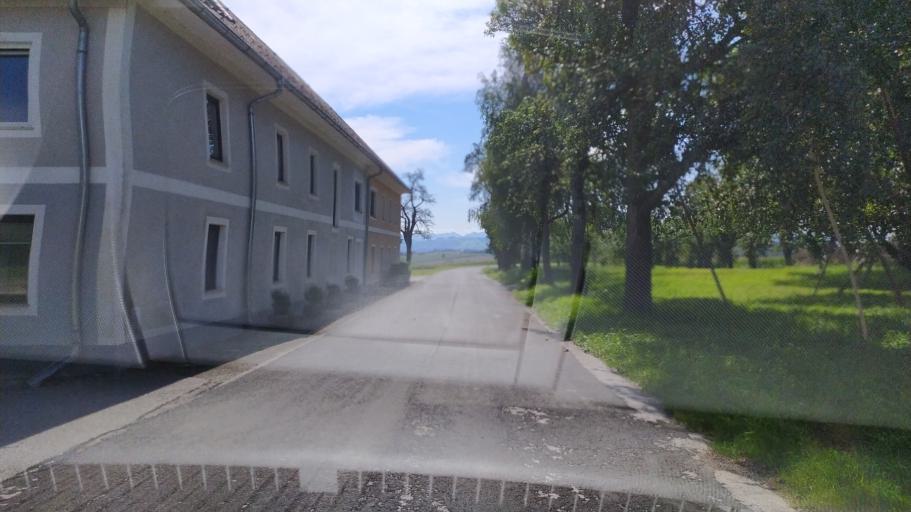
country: AT
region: Lower Austria
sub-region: Politischer Bezirk Amstetten
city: Strengberg
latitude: 48.1140
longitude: 14.6573
